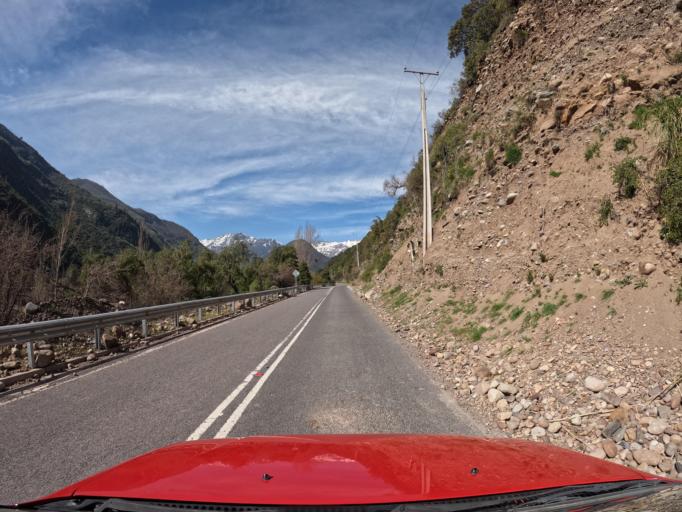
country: CL
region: O'Higgins
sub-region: Provincia de Colchagua
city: Chimbarongo
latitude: -35.0005
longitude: -70.7998
